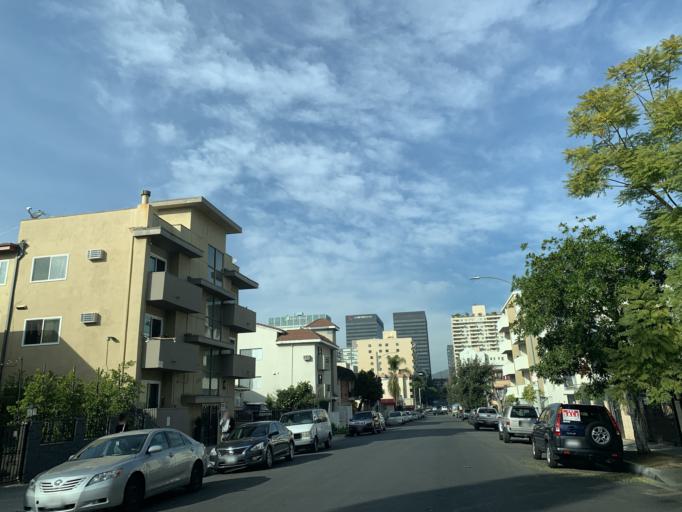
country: US
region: California
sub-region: Los Angeles County
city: Silver Lake
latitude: 34.0560
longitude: -118.3020
